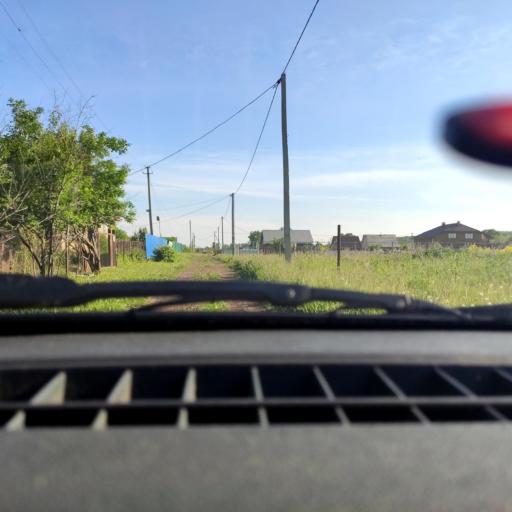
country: RU
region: Bashkortostan
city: Avdon
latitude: 54.4621
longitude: 55.8190
